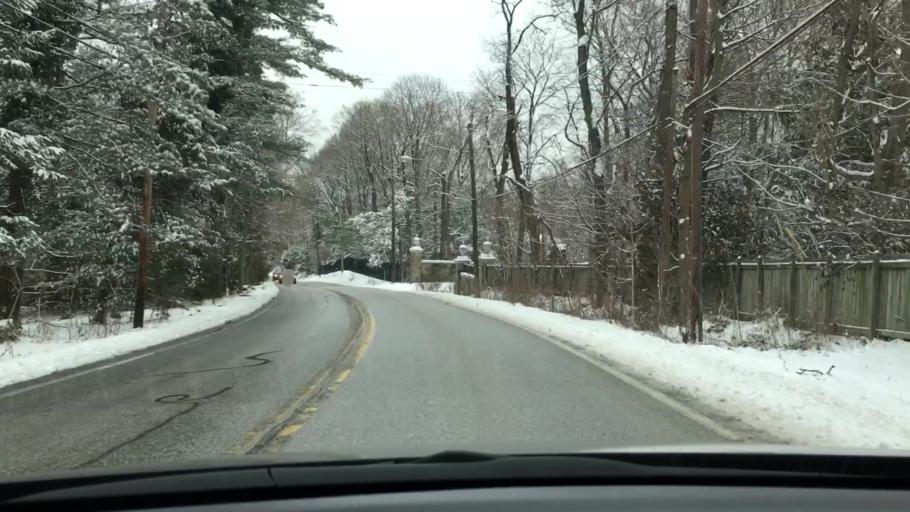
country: US
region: Pennsylvania
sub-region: York County
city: Grantley
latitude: 39.9401
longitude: -76.7295
